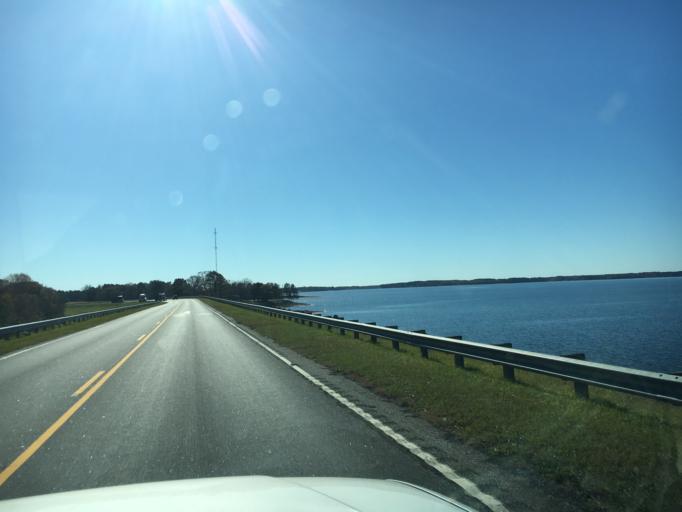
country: US
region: Georgia
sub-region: Hart County
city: Hartwell
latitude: 34.3711
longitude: -82.8143
